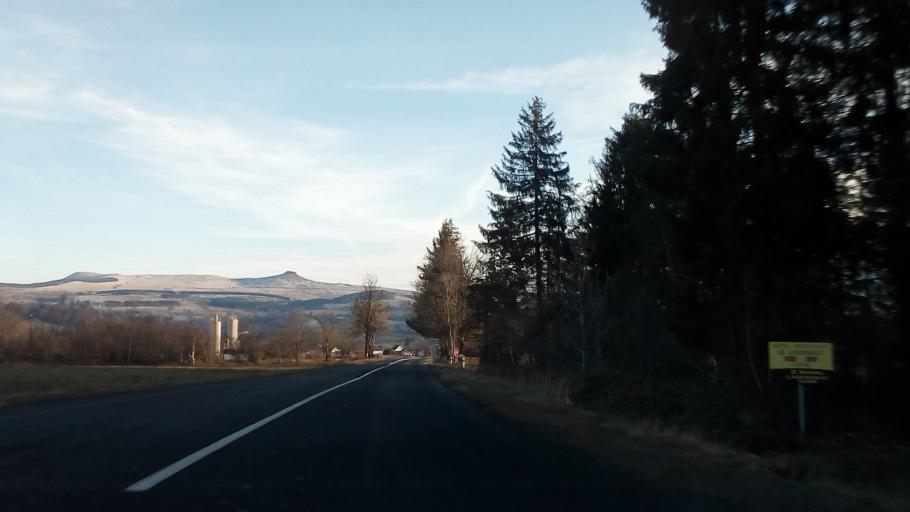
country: FR
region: Auvergne
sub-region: Departement du Puy-de-Dome
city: Saint-Sauves-d'Auvergne
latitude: 45.6535
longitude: 2.6996
